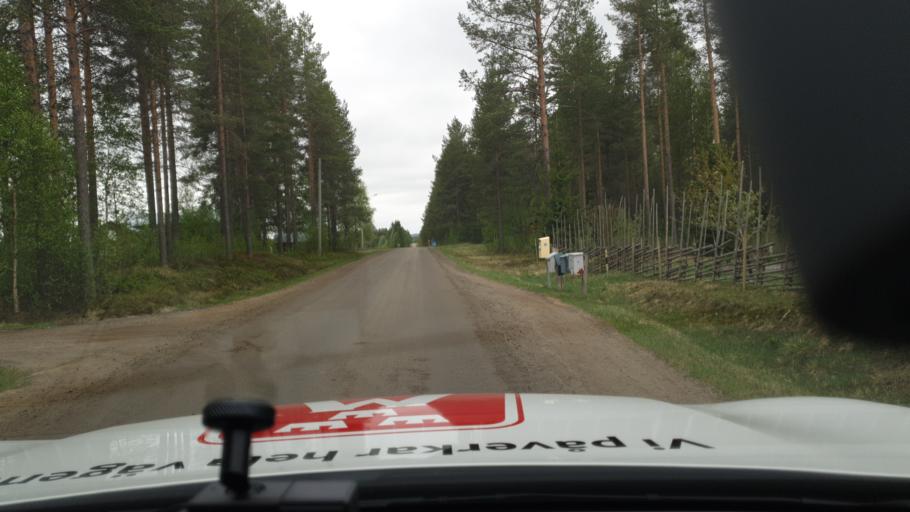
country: SE
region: Vaesterbotten
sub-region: Vannas Kommun
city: Vannasby
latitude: 64.0482
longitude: 19.9126
